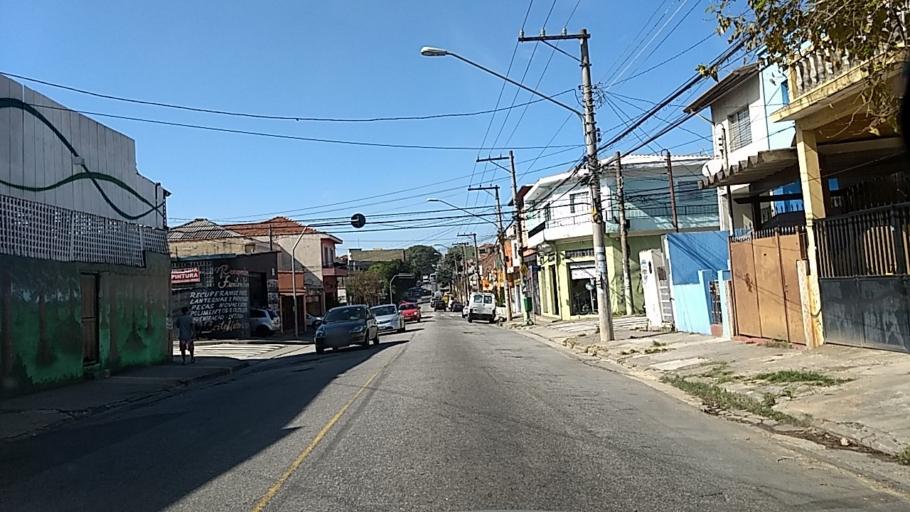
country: BR
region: Sao Paulo
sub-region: Guarulhos
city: Guarulhos
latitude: -23.4818
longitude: -46.5922
